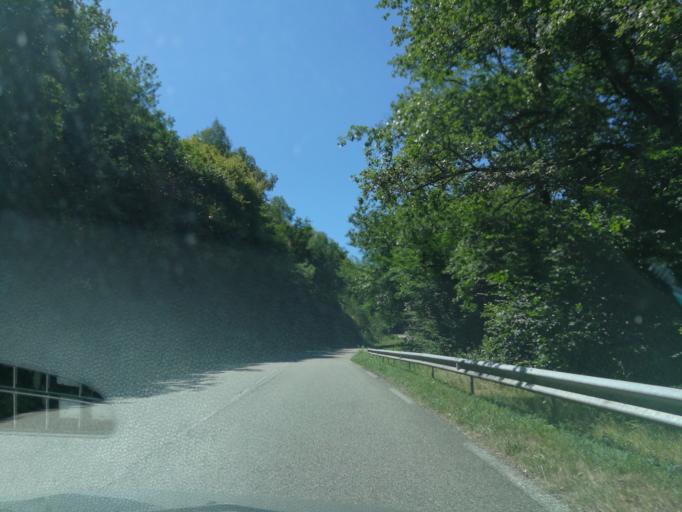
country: FR
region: Limousin
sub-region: Departement de la Correze
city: Argentat
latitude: 45.0606
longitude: 1.9457
